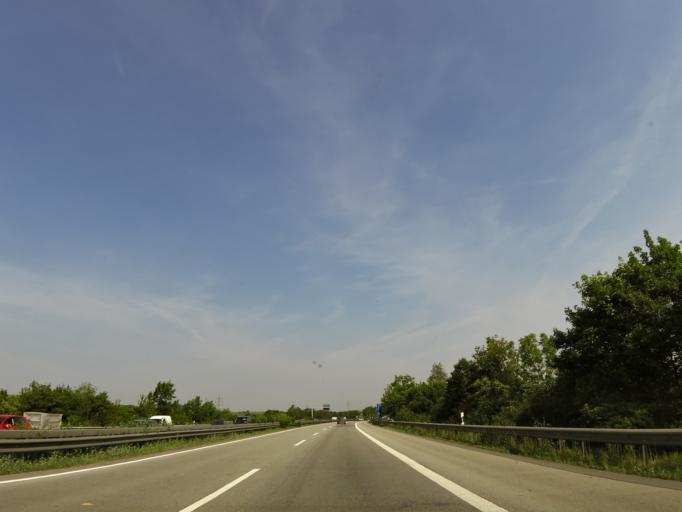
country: DE
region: Rheinland-Pfalz
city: Albig
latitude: 49.7603
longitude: 8.1175
